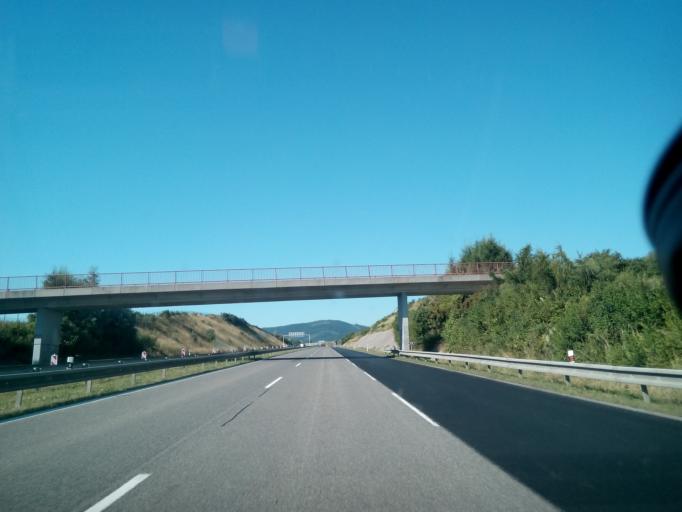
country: SK
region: Kosicky
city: Krompachy
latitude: 49.0060
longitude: 20.9356
